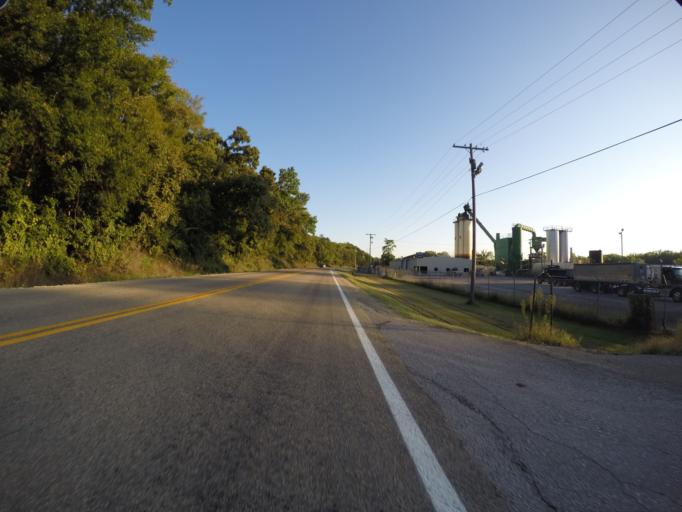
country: US
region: Kansas
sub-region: Riley County
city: Manhattan
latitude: 39.1690
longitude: -96.5535
